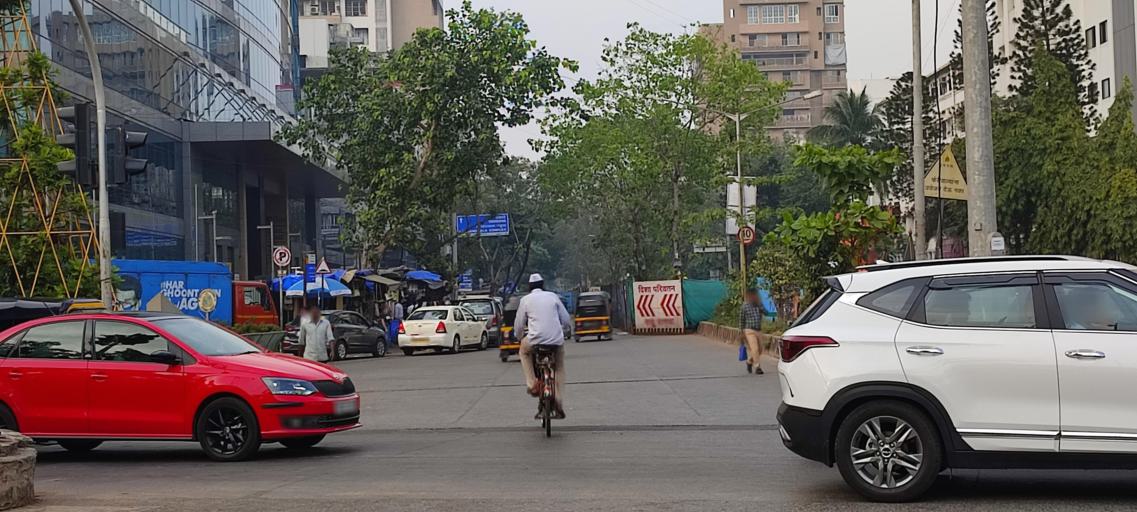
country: IN
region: Maharashtra
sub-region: Mumbai Suburban
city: Mumbai
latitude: 19.1025
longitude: 72.8368
